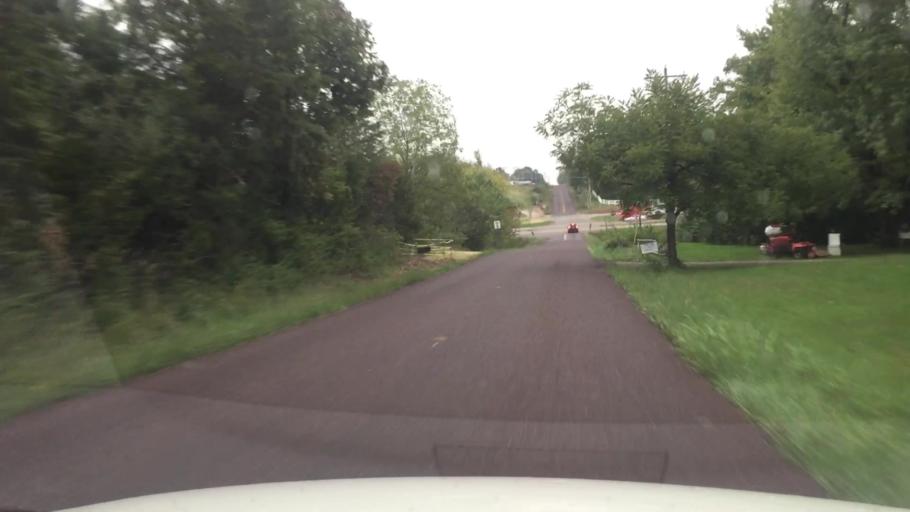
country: US
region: Missouri
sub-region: Boone County
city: Ashland
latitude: 38.8106
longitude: -92.2535
